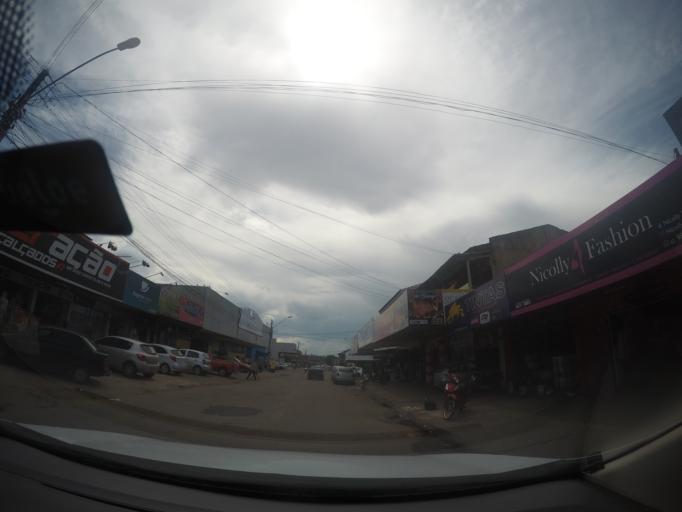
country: BR
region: Goias
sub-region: Goiania
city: Goiania
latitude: -16.6958
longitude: -49.3562
